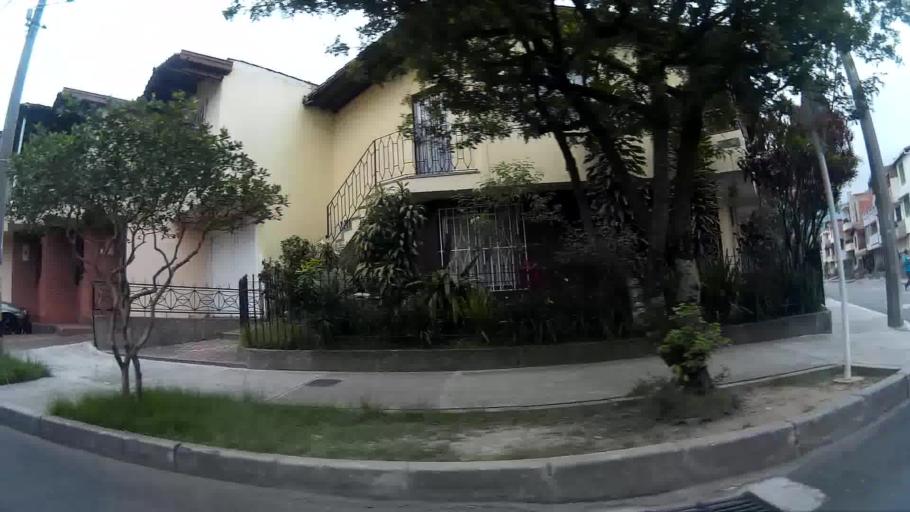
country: CO
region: Antioquia
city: Medellin
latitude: 6.2222
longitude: -75.5875
